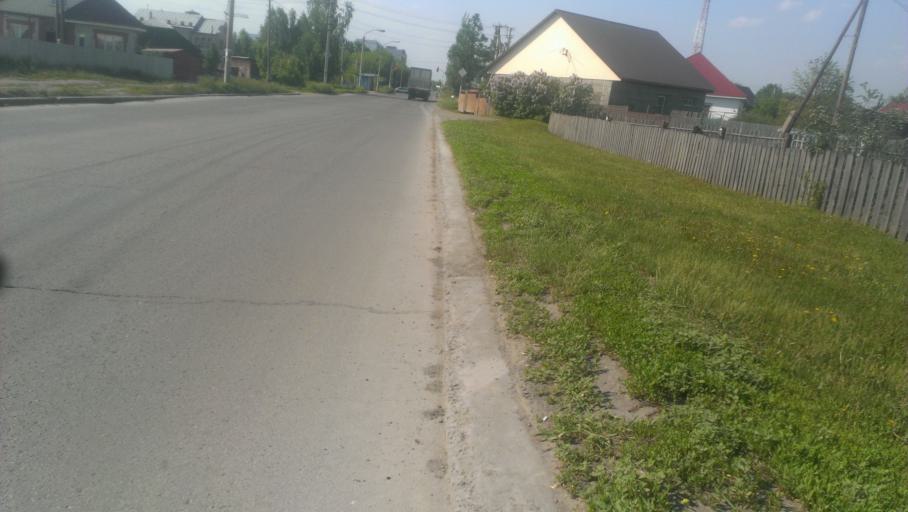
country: RU
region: Altai Krai
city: Novoaltaysk
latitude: 53.4057
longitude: 83.9448
